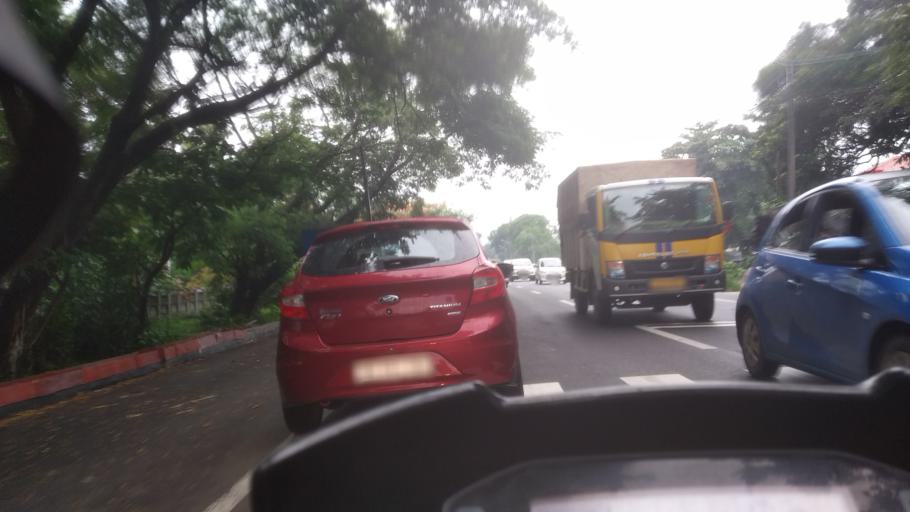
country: IN
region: Kerala
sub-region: Alappuzha
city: Kayankulam
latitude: 9.1872
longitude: 76.4886
